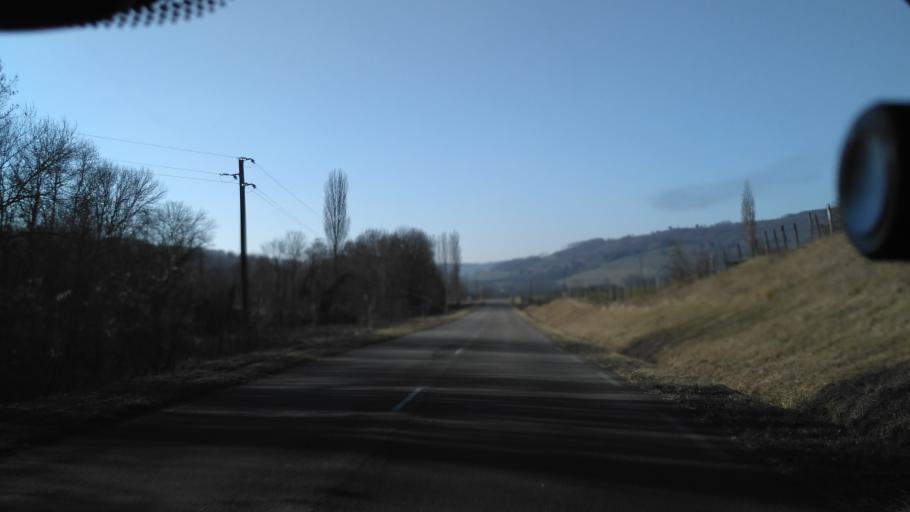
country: FR
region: Rhone-Alpes
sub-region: Departement de la Drome
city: Saint-Paul-les-Romans
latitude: 45.1527
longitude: 5.1341
